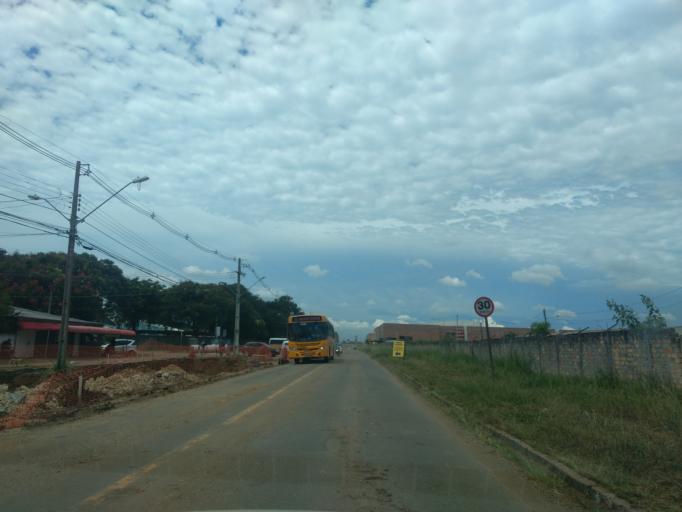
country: BR
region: Parana
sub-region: Pinhais
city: Pinhais
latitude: -25.4233
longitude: -49.2163
